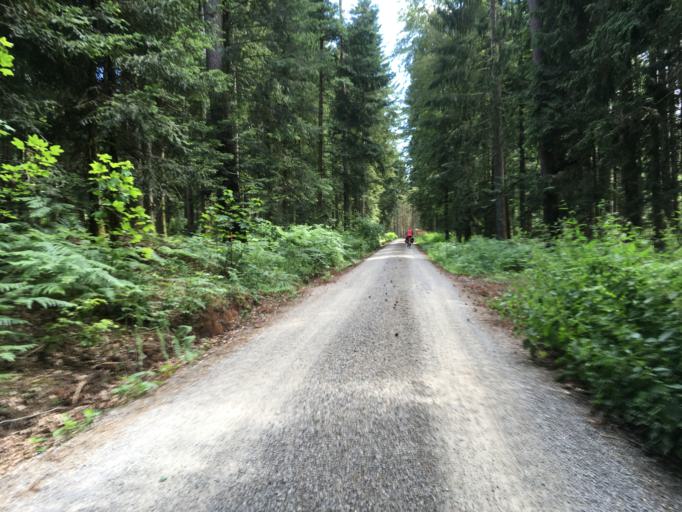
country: DE
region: Baden-Wuerttemberg
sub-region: Karlsruhe Region
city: Baiersbronn
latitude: 48.5595
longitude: 8.4222
